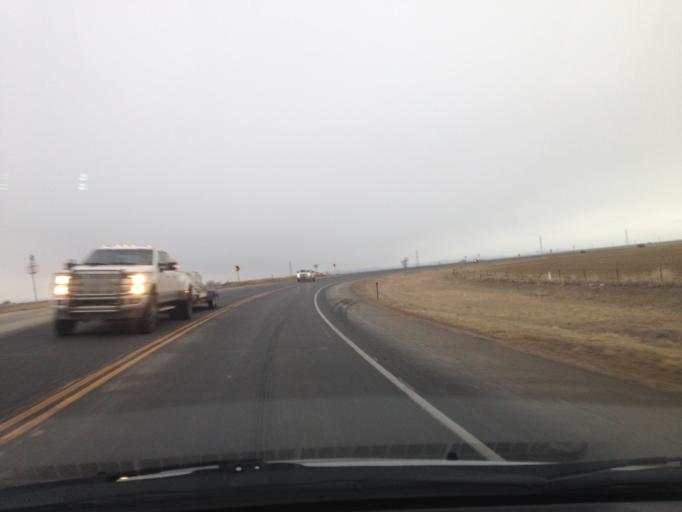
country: US
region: Colorado
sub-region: Weld County
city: Dacono
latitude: 40.0801
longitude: -104.9004
